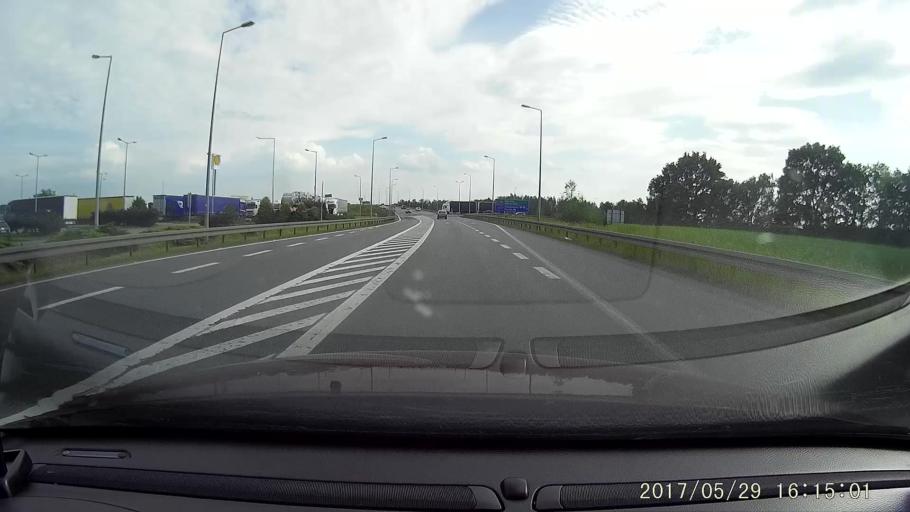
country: PL
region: Lower Silesian Voivodeship
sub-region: Powiat zgorzelecki
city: Lagow
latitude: 51.1770
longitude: 15.0312
